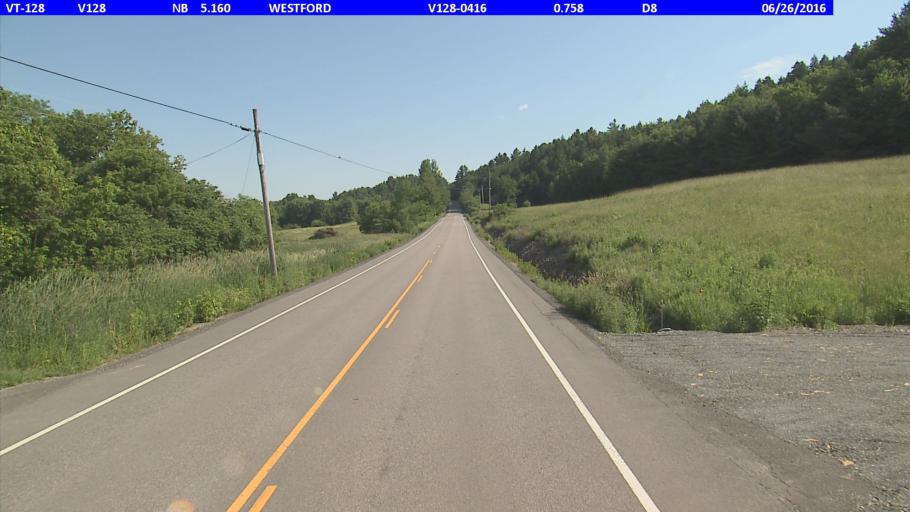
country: US
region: Vermont
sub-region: Chittenden County
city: Jericho
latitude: 44.5692
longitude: -73.0224
